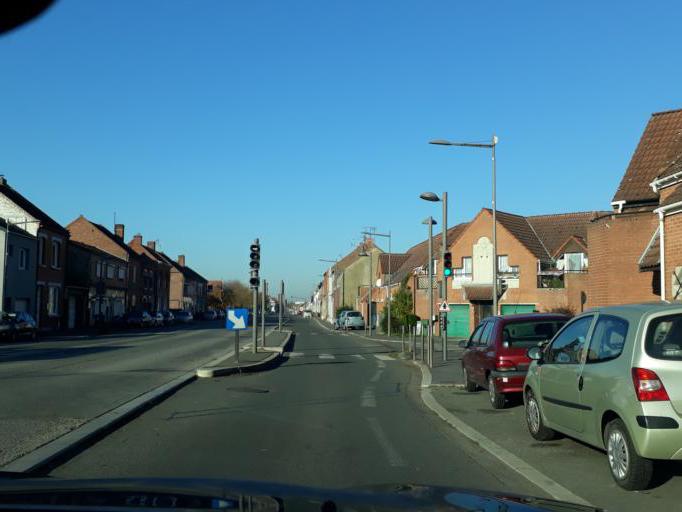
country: FR
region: Nord-Pas-de-Calais
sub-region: Departement du Nord
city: Sin-le-Noble
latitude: 50.3505
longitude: 3.1355
